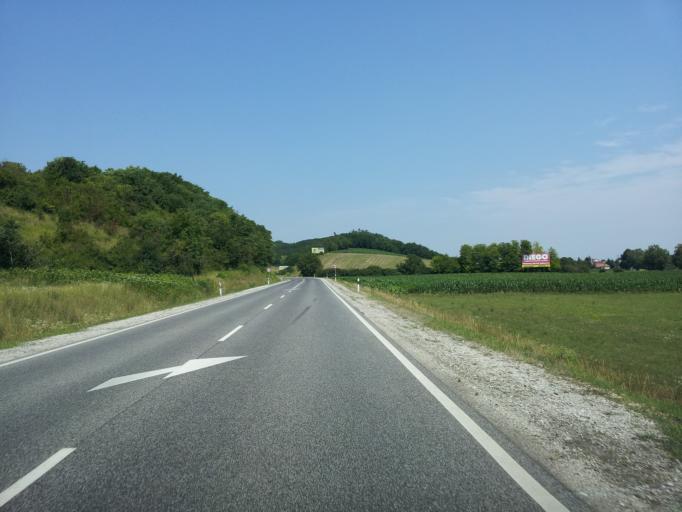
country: HU
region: Zala
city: Zalaegerszeg
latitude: 46.8391
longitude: 16.9274
